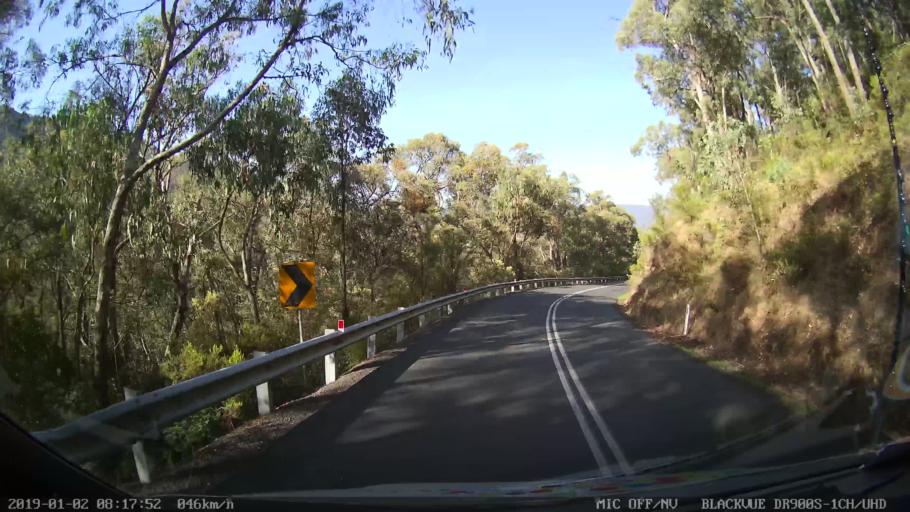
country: AU
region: New South Wales
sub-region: Tumut Shire
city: Tumut
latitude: -35.5812
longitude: 148.3208
